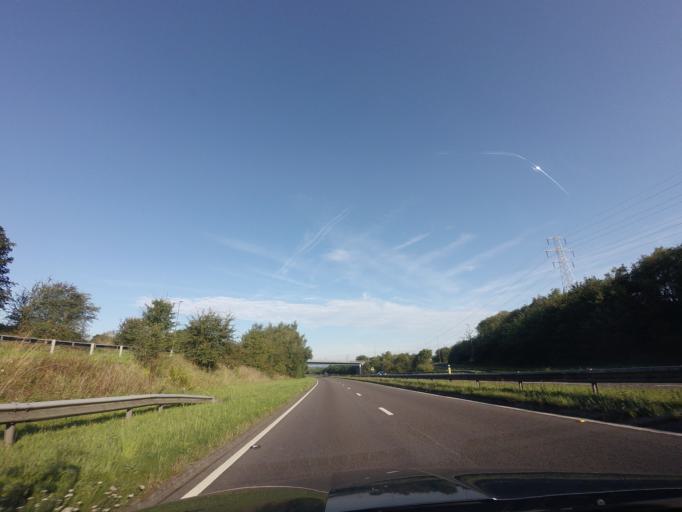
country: GB
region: England
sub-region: Derbyshire
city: Chesterfield
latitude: 53.2078
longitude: -1.3764
